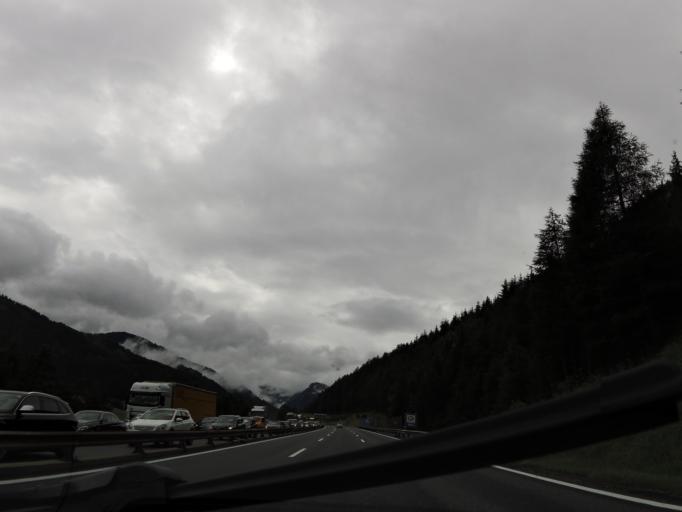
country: AT
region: Tyrol
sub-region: Politischer Bezirk Innsbruck Land
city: Steinach am Brenner
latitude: 47.1060
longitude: 11.4554
